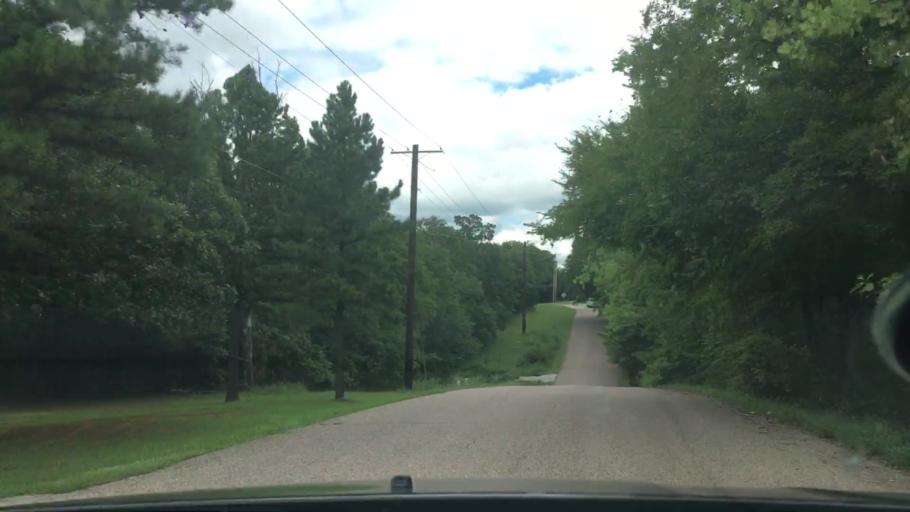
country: US
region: Oklahoma
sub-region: Pontotoc County
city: Ada
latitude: 34.7553
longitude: -96.6524
